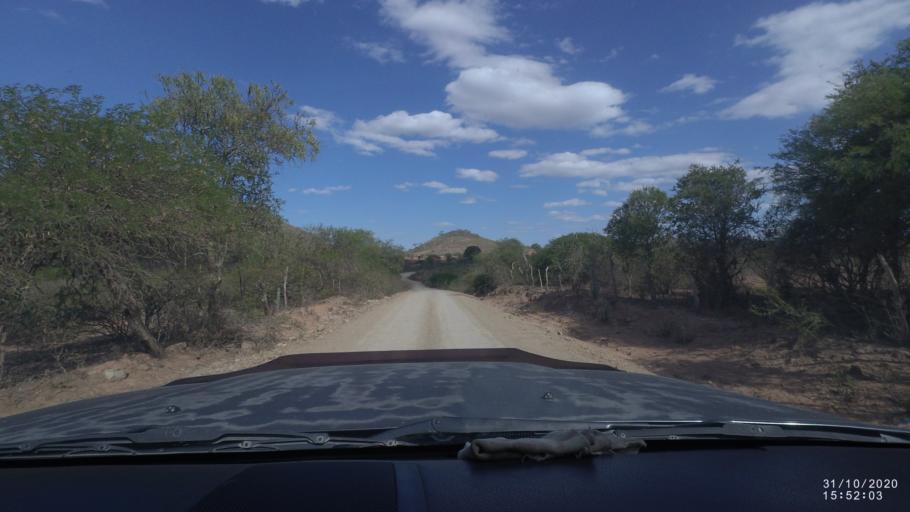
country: BO
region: Chuquisaca
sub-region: Provincia Zudanez
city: Mojocoya
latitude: -18.3175
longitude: -64.6969
